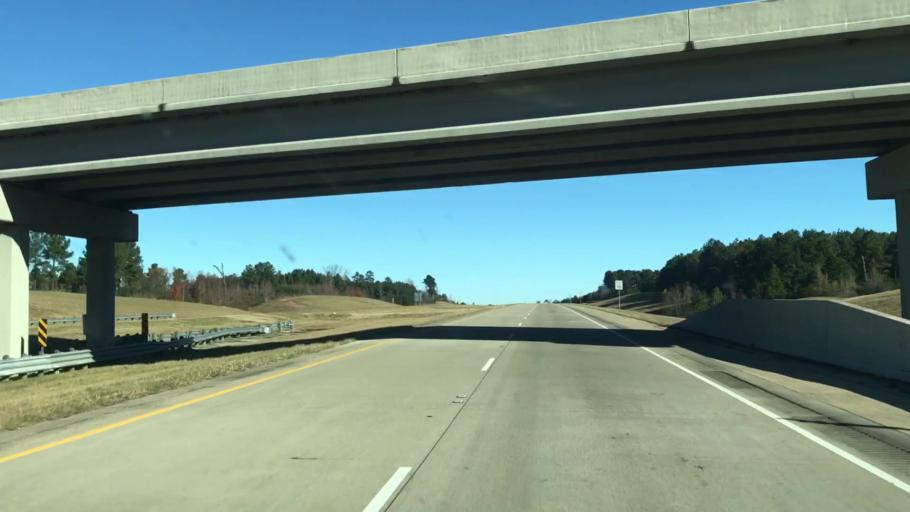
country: US
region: Louisiana
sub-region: Caddo Parish
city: Vivian
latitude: 33.0076
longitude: -93.9051
